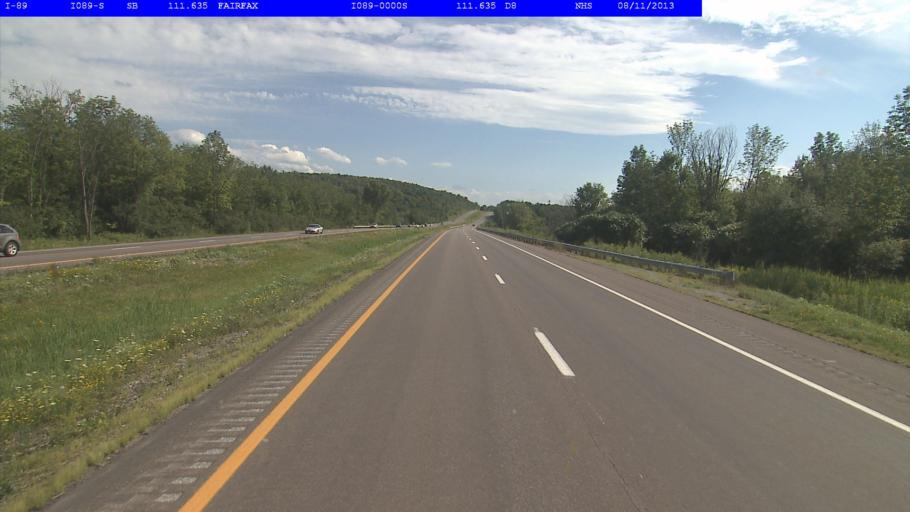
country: US
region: Vermont
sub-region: Franklin County
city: Saint Albans
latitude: 44.7648
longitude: -73.0762
